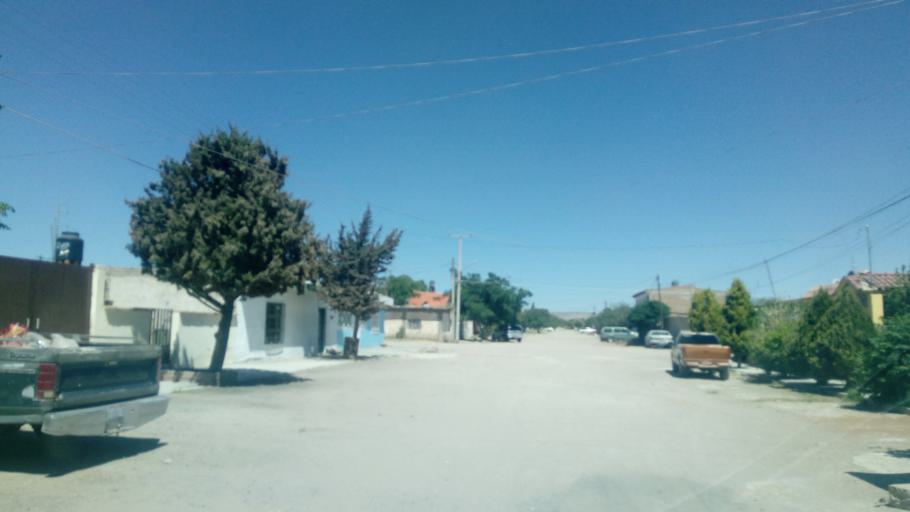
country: MX
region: Durango
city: Victoria de Durango
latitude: 24.0769
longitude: -104.6577
